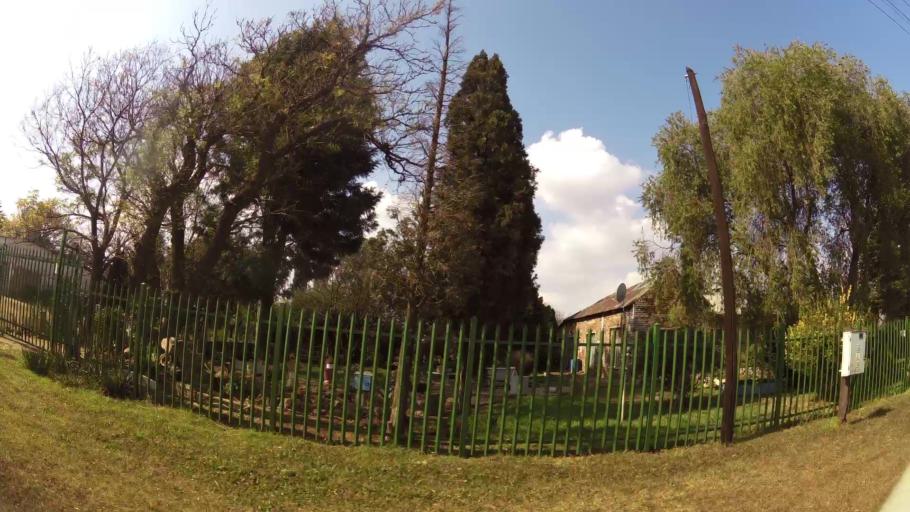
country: ZA
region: Mpumalanga
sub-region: Nkangala District Municipality
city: Delmas
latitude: -26.1899
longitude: 28.5450
